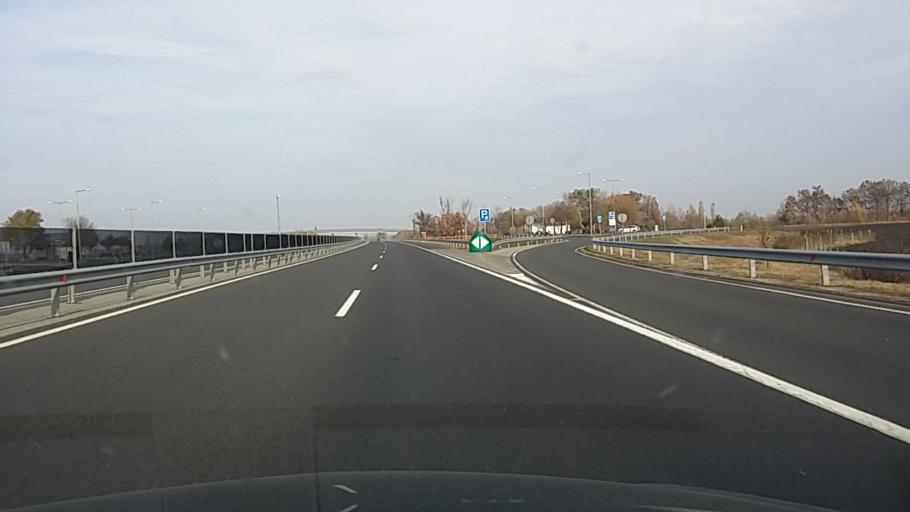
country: HU
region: Hajdu-Bihar
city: Gorbehaza
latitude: 47.8241
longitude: 21.3239
